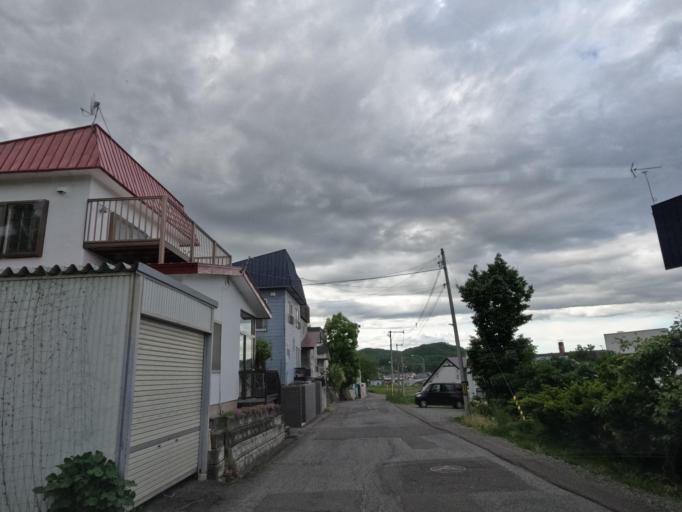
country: JP
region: Hokkaido
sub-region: Asahikawa-shi
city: Asahikawa
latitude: 43.7706
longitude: 142.3118
